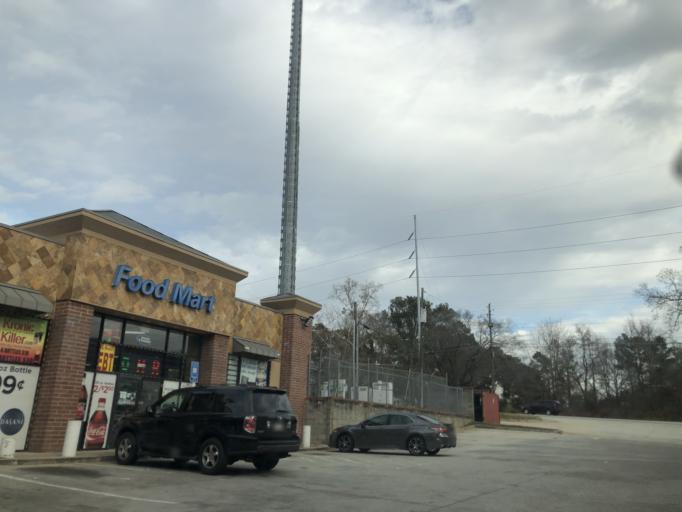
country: US
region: Georgia
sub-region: DeKalb County
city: Pine Mountain
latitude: 33.6716
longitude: -84.1798
